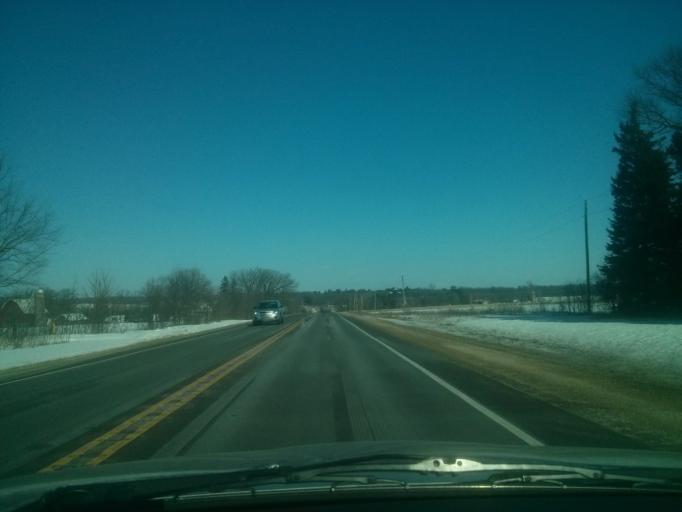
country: US
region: Wisconsin
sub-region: Polk County
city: Clear Lake
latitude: 45.1615
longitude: -92.2824
